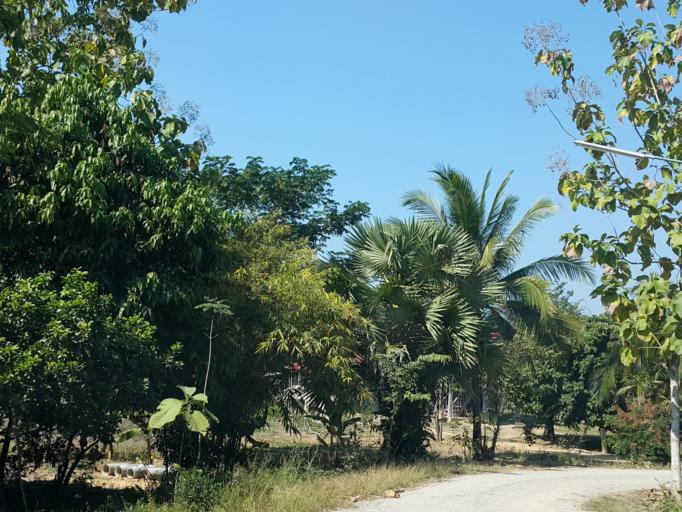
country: TH
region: Sukhothai
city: Thung Saliam
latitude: 17.3442
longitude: 99.4421
